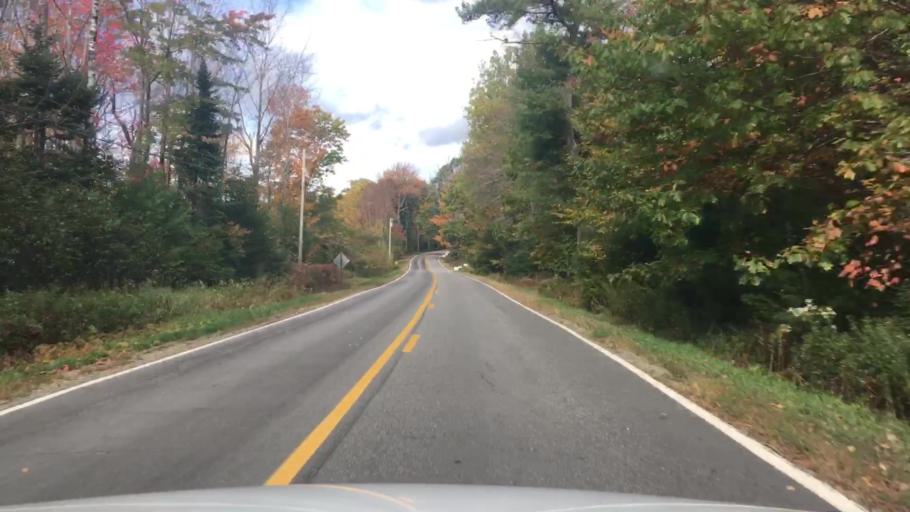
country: US
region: Maine
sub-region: Knox County
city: Hope
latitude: 44.3116
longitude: -69.1169
